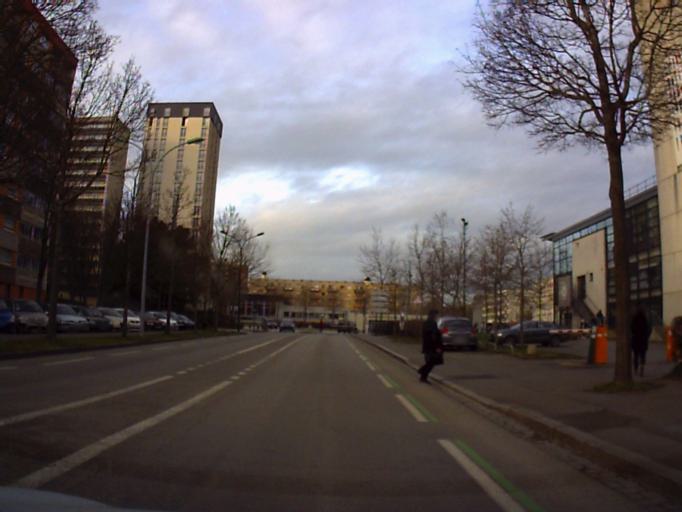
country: FR
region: Brittany
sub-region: Departement d'Ille-et-Vilaine
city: Rennes
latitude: 48.1204
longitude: -1.7045
